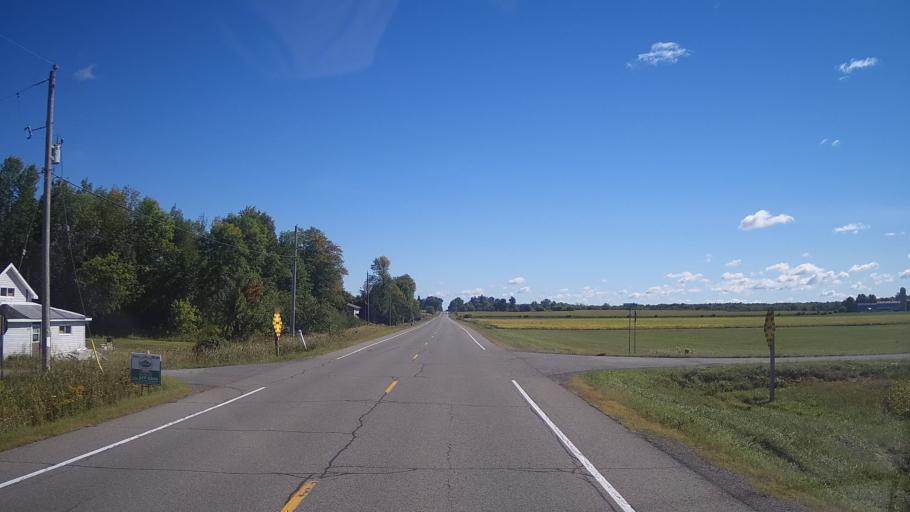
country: US
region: New York
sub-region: St. Lawrence County
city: Ogdensburg
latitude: 44.9343
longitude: -75.3220
